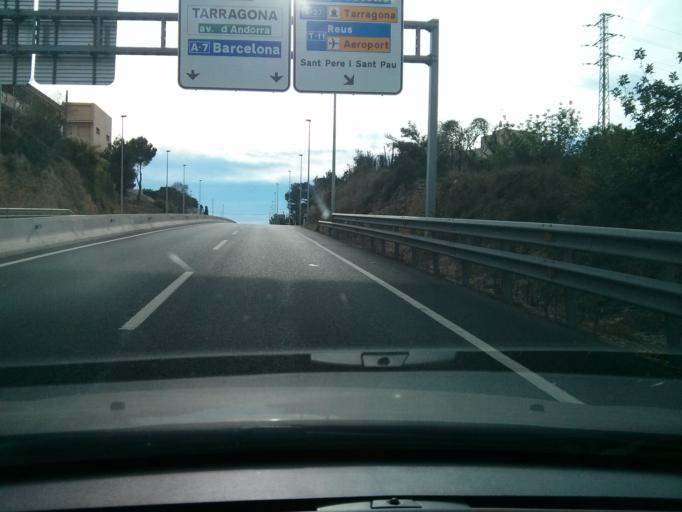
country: ES
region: Catalonia
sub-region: Provincia de Tarragona
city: Tarragona
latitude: 41.1348
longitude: 1.2382
